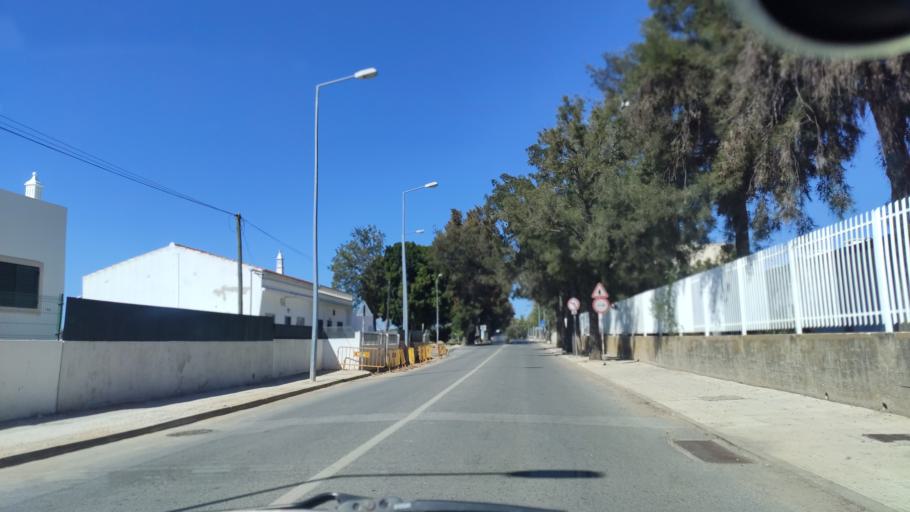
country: PT
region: Faro
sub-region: Olhao
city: Olhao
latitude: 37.0381
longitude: -7.8503
